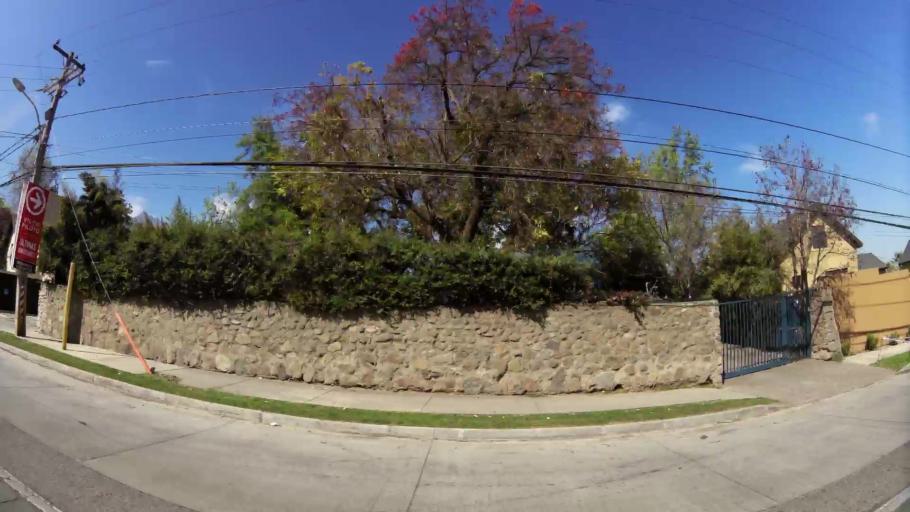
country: CL
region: Santiago Metropolitan
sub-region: Provincia de Santiago
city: Villa Presidente Frei, Nunoa, Santiago, Chile
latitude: -33.4325
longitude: -70.5307
